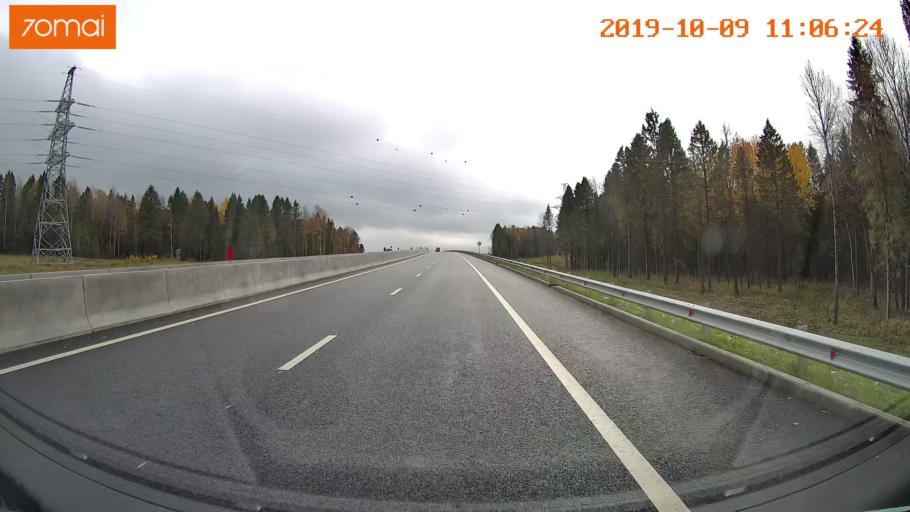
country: RU
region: Vologda
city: Vologda
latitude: 59.1870
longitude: 39.7602
